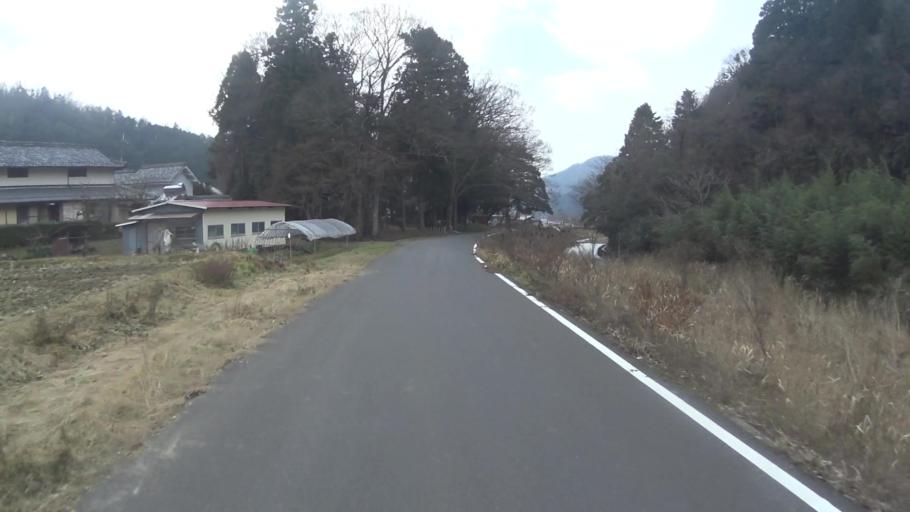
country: JP
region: Kyoto
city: Maizuru
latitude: 35.4442
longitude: 135.4327
